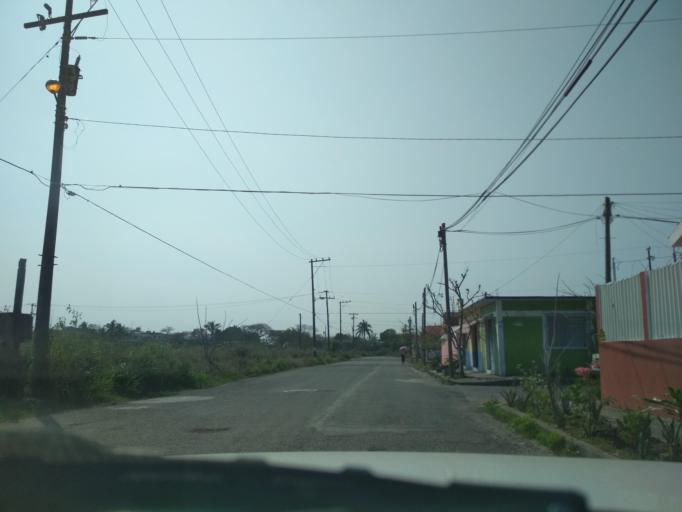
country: MX
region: Veracruz
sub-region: Veracruz
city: Colonia el Renacimiento
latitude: 19.2207
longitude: -96.2115
